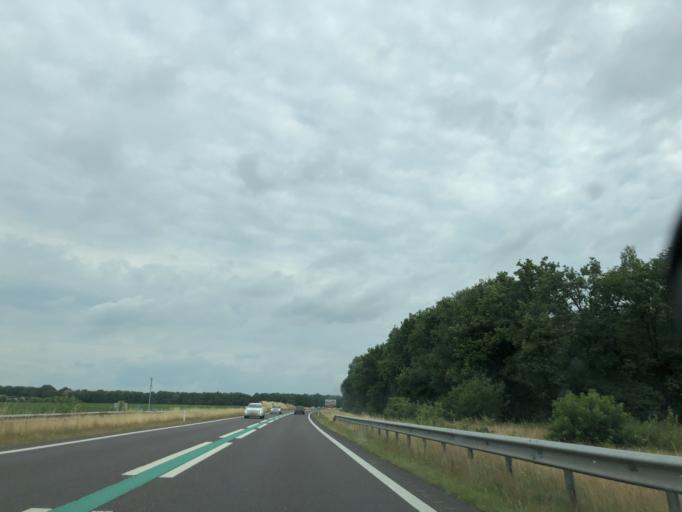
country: NL
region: Drenthe
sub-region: Gemeente Aa en Hunze
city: Anloo
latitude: 53.0618
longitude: 6.7026
